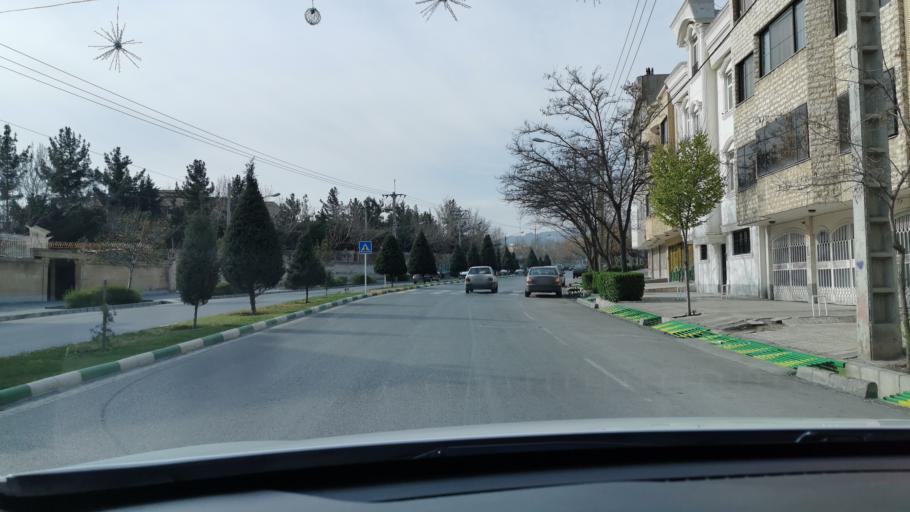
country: IR
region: Razavi Khorasan
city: Mashhad
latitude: 36.3111
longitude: 59.5160
